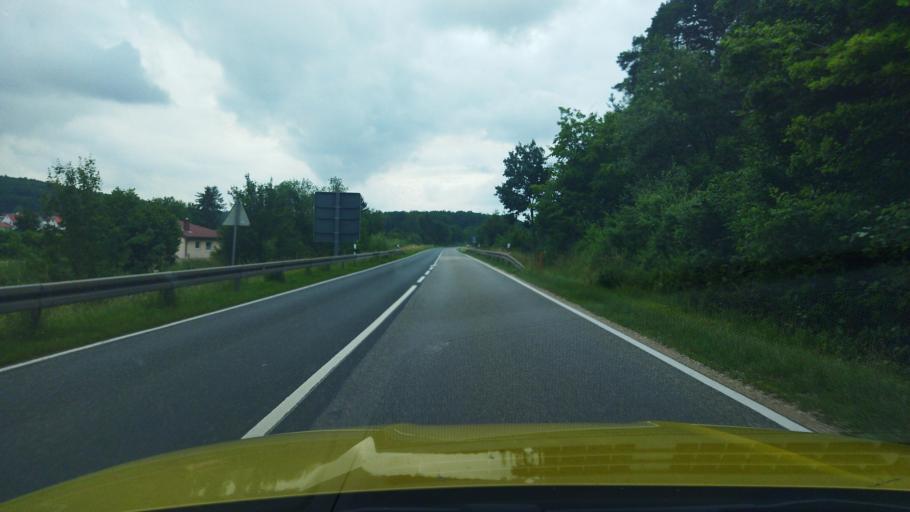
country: DE
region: Bavaria
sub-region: Regierungsbezirk Mittelfranken
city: Gunzenhausen
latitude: 49.1255
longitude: 10.7981
